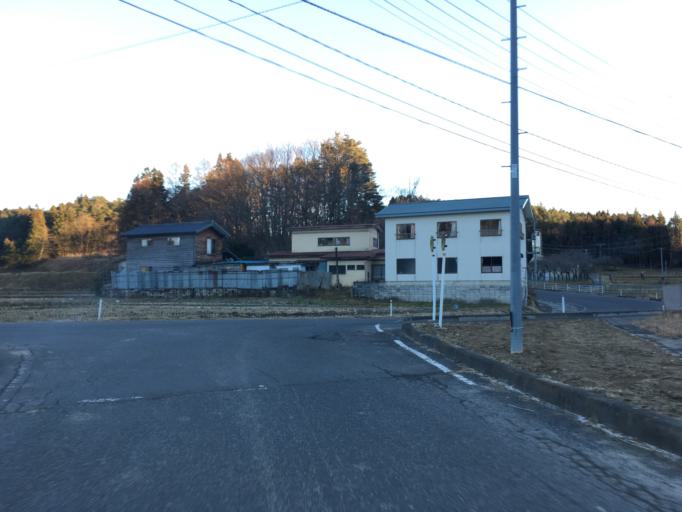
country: JP
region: Fukushima
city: Ishikawa
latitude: 37.1959
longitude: 140.5574
